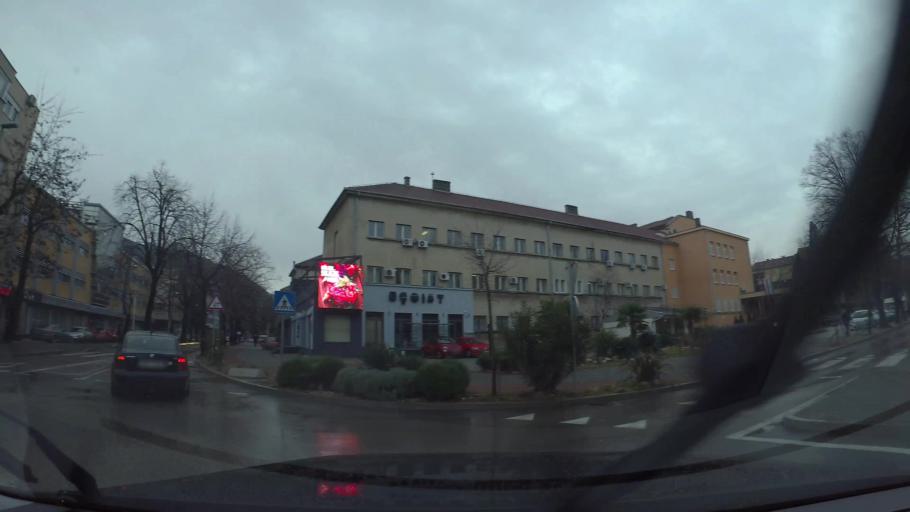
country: BA
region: Federation of Bosnia and Herzegovina
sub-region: Hercegovacko-Bosanski Kanton
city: Mostar
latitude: 43.3457
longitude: 17.8042
